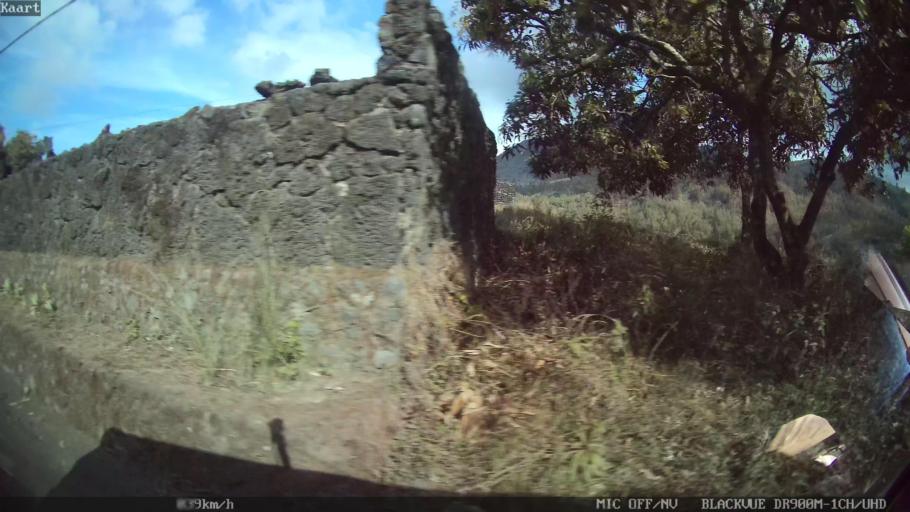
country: ID
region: Bali
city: Banjar Kedisan
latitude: -8.2167
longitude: 115.3679
